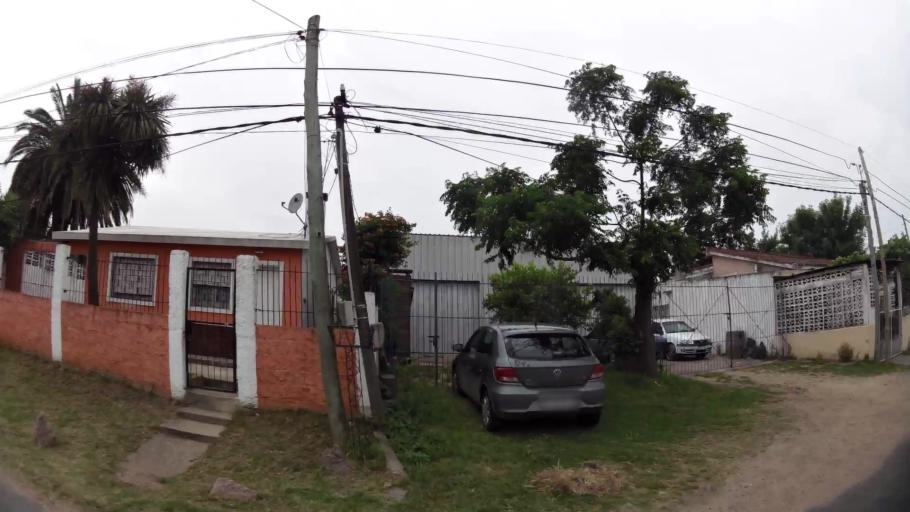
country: UY
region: Canelones
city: Las Piedras
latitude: -34.7361
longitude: -56.2276
